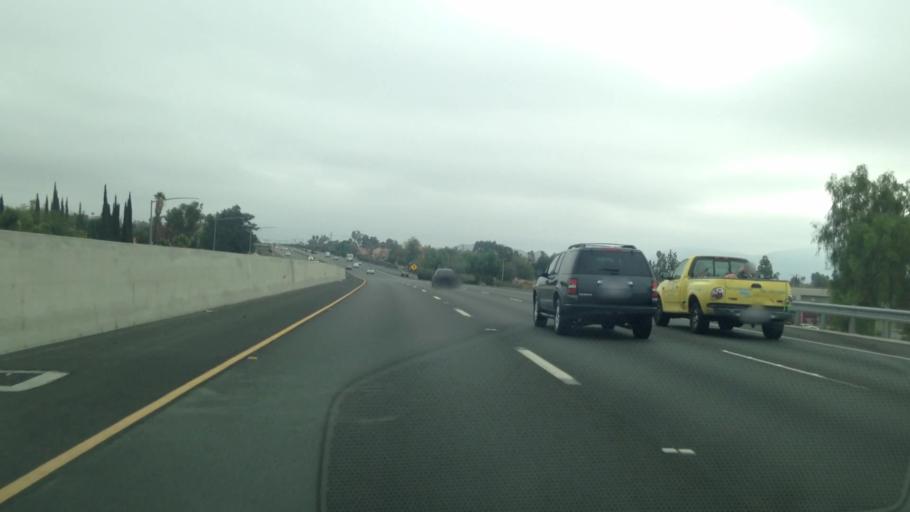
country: US
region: California
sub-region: Riverside County
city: Moreno Valley
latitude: 33.9395
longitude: -117.2254
